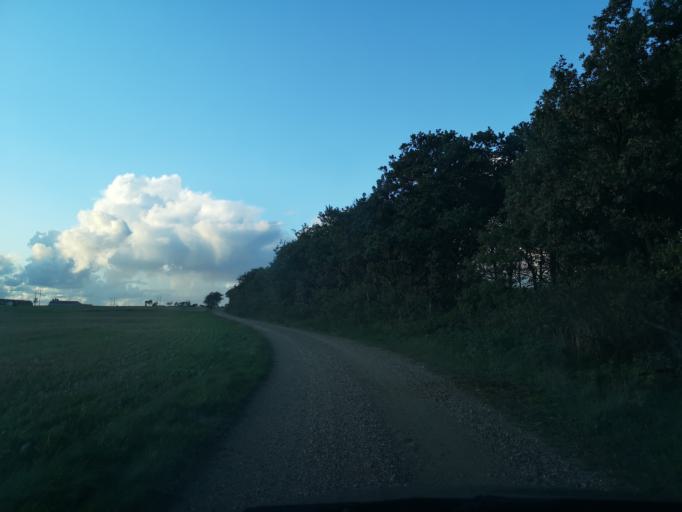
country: DK
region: Central Jutland
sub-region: Ringkobing-Skjern Kommune
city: Videbaek
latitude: 56.0440
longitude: 8.5885
